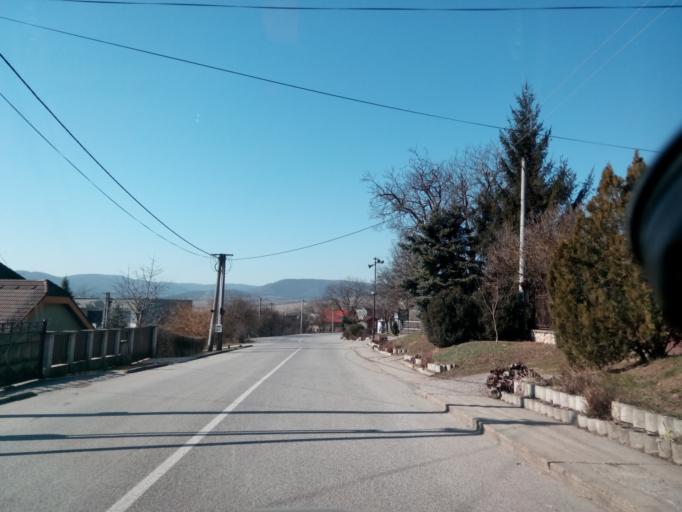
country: SK
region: Kosicky
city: Roznava
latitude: 48.5942
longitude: 20.6771
